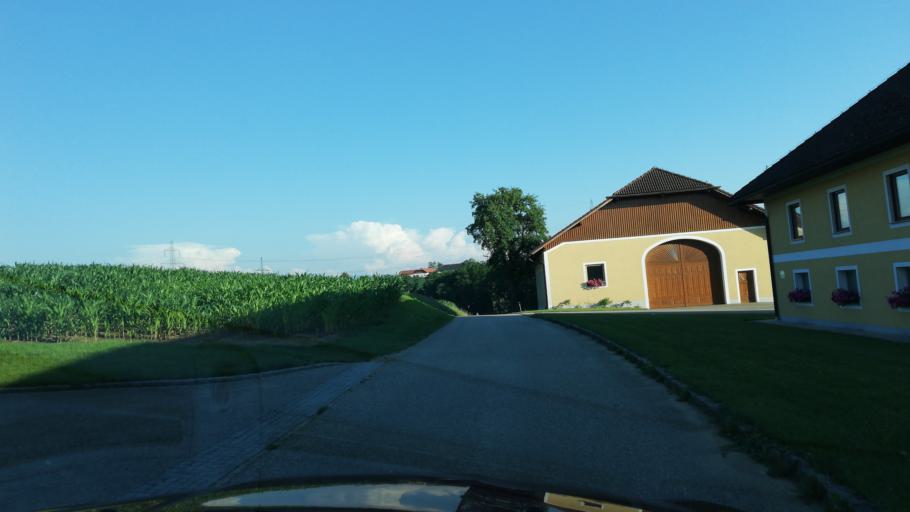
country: AT
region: Upper Austria
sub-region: Wels-Land
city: Steinhaus
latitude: 48.0875
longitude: 14.0278
